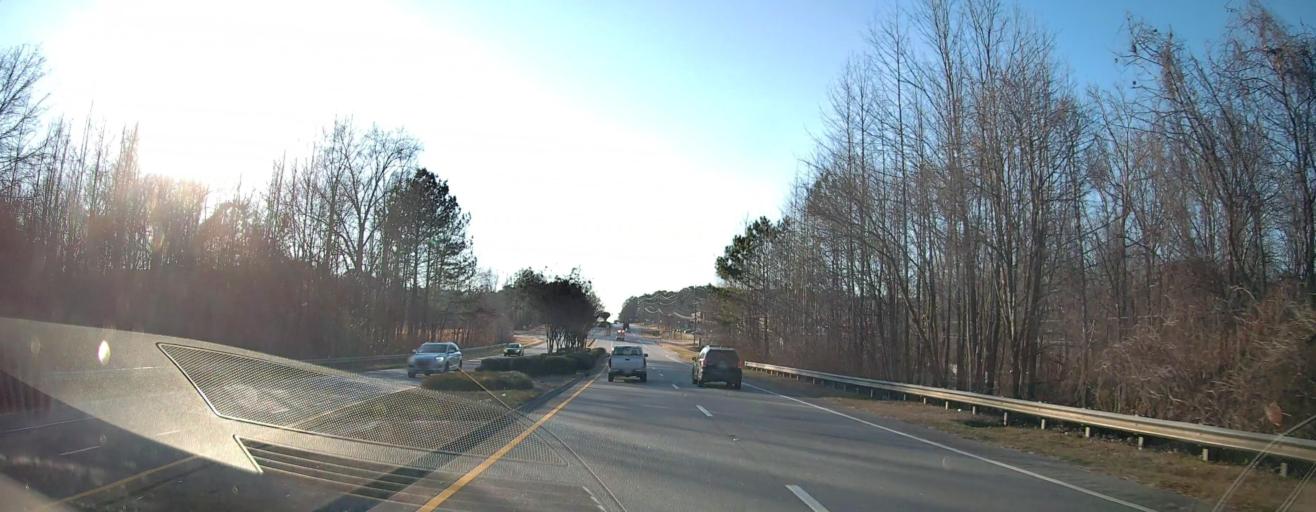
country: US
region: Georgia
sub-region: Fayette County
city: Fayetteville
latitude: 33.4482
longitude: -84.4800
